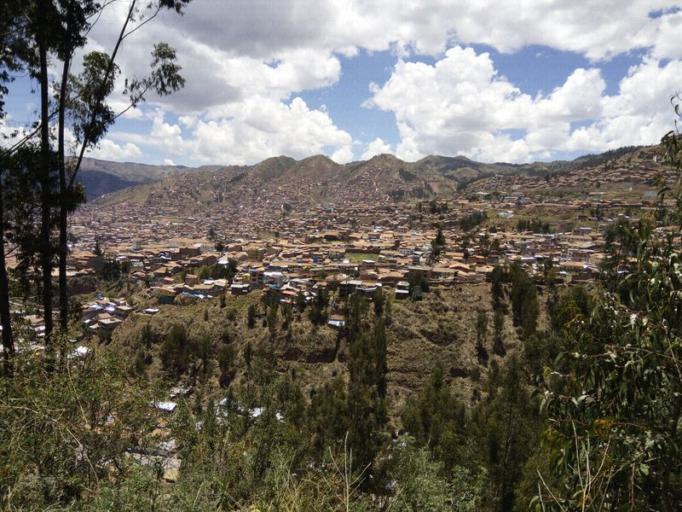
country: PE
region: Cusco
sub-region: Provincia de Cusco
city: Cusco
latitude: -13.5090
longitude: -71.9844
